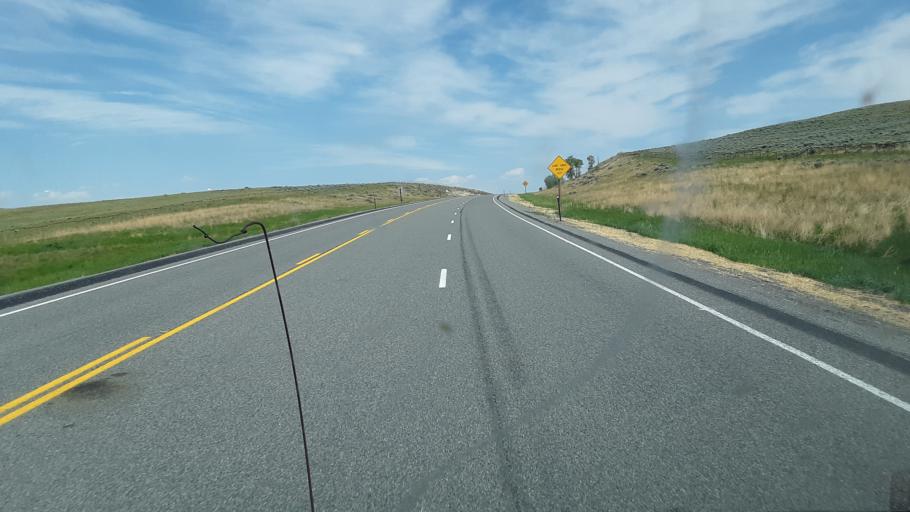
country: US
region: Wyoming
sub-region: Park County
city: Cody
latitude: 44.2588
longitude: -108.8681
